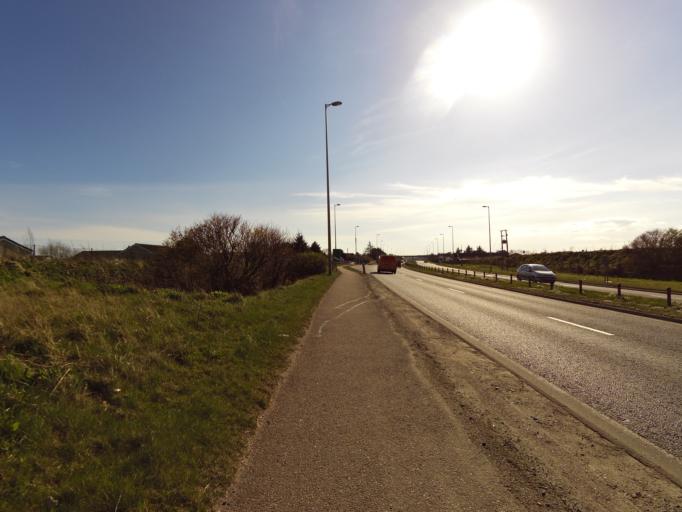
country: GB
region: Scotland
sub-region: Aberdeenshire
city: Newtonhill
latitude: 57.0340
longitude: -2.1546
